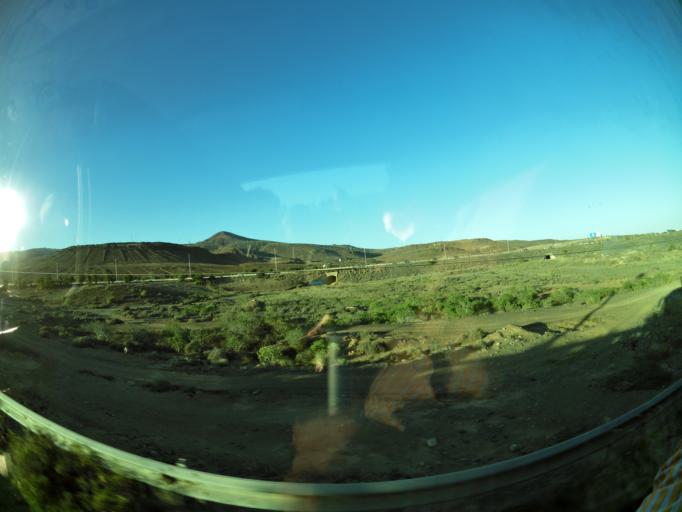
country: ES
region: Canary Islands
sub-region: Provincia de Las Palmas
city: Playa del Ingles
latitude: 27.7855
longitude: -15.5146
